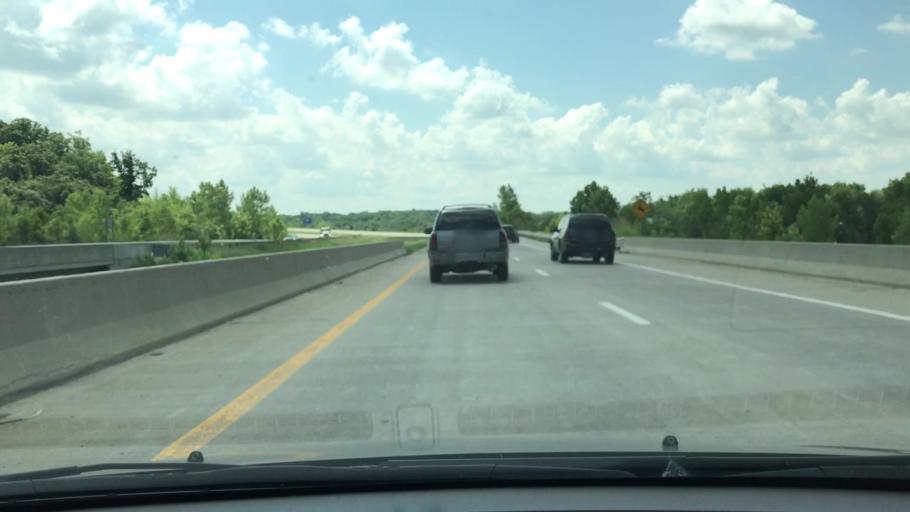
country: US
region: Missouri
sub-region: Jackson County
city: Grandview
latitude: 38.8678
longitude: -94.6012
